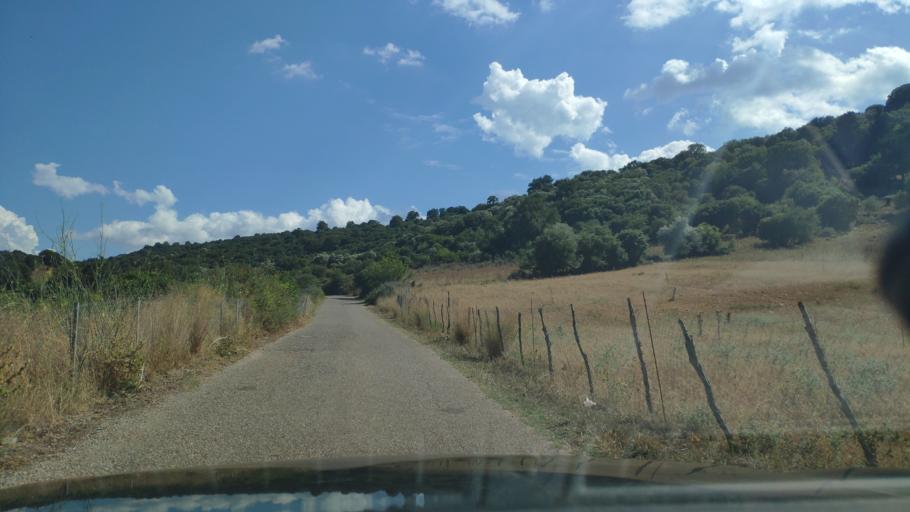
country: GR
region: West Greece
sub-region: Nomos Aitolias kai Akarnanias
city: Katouna
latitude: 38.8160
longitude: 21.1054
